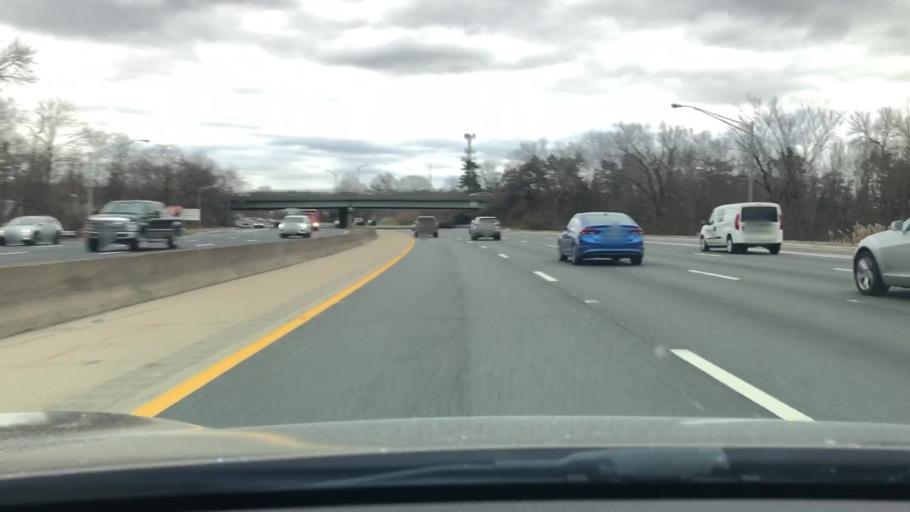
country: US
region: New Jersey
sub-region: Passaic County
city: Totowa
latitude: 40.8971
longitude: -74.2250
